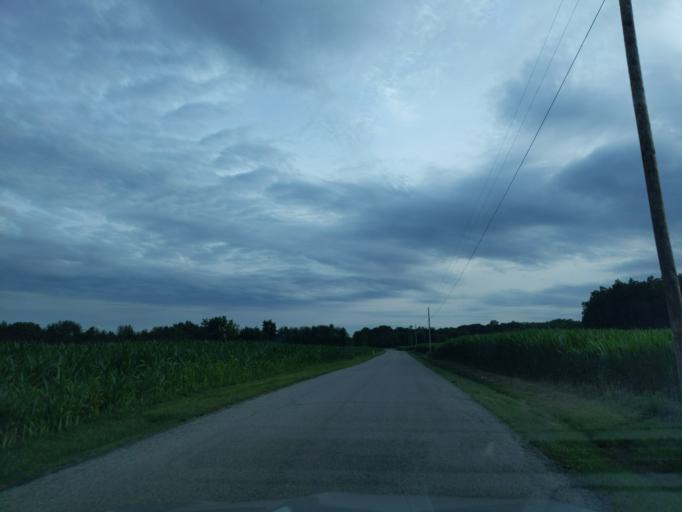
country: US
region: Indiana
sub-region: Ripley County
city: Sunman
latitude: 39.3020
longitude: -85.0860
